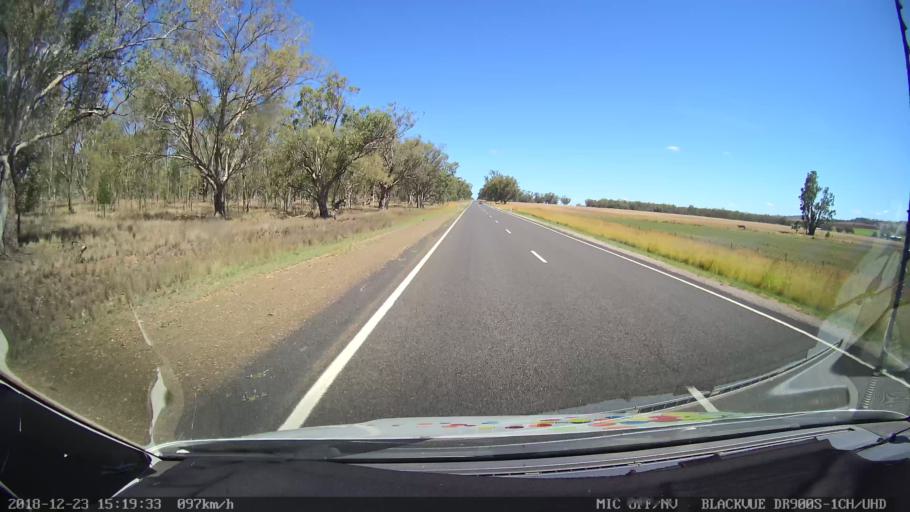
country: AU
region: New South Wales
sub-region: Tamworth Municipality
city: Manilla
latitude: -30.8306
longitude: 150.7836
